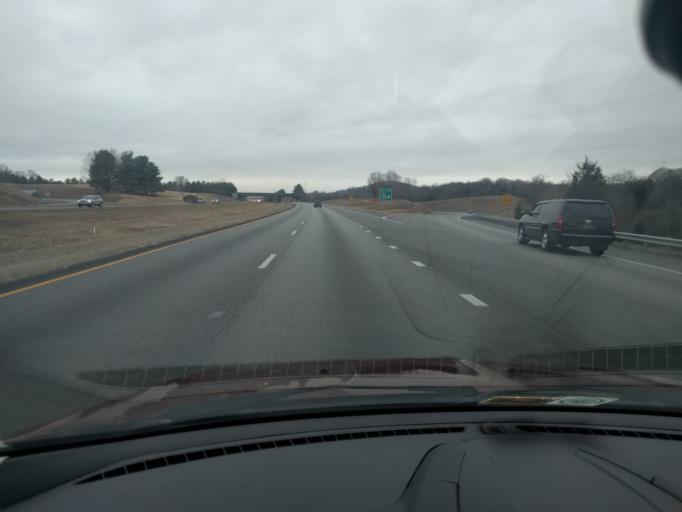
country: US
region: Virginia
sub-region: Augusta County
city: Jolivue
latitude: 38.1245
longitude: -79.0438
